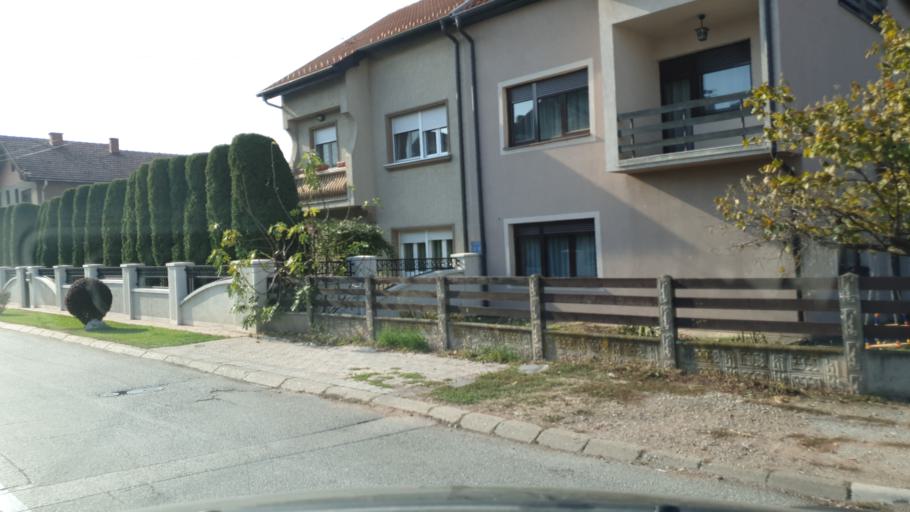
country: RS
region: Central Serbia
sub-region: Pomoravski Okrug
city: Paracin
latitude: 43.8599
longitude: 21.4249
